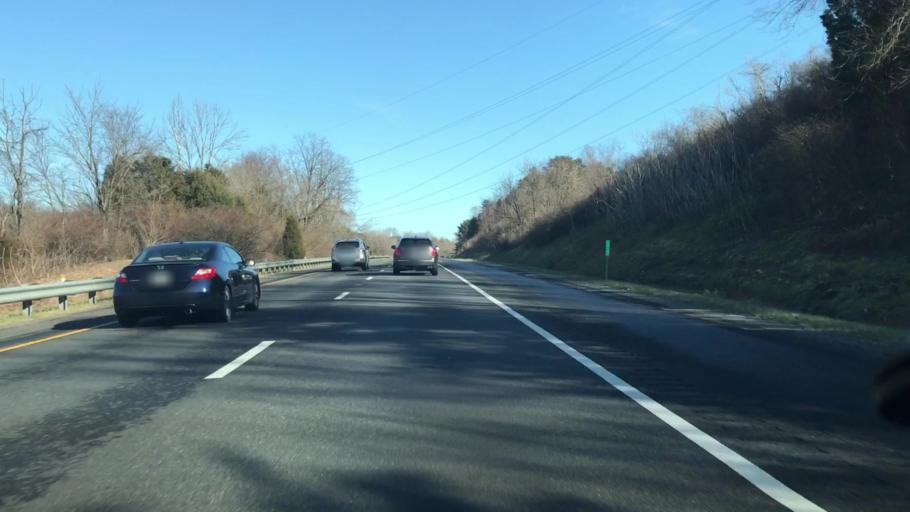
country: US
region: Virginia
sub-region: Botetourt County
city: Daleville
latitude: 37.4006
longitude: -79.8974
